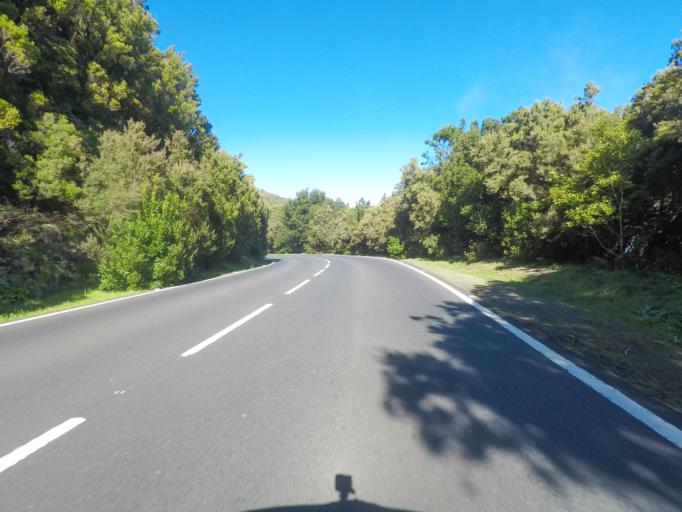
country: ES
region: Canary Islands
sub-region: Provincia de Santa Cruz de Tenerife
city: Alajero
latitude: 28.1073
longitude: -17.2386
